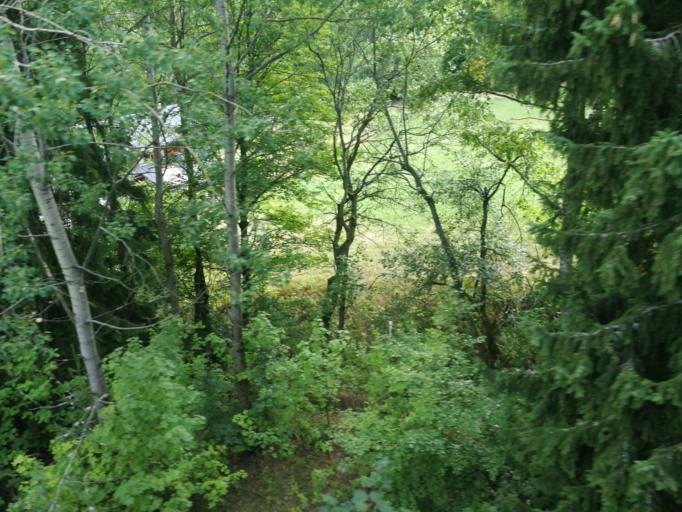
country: CZ
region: Kralovehradecky
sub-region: Okres Trutnov
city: Svoboda nad Upou
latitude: 50.6338
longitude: 15.7674
